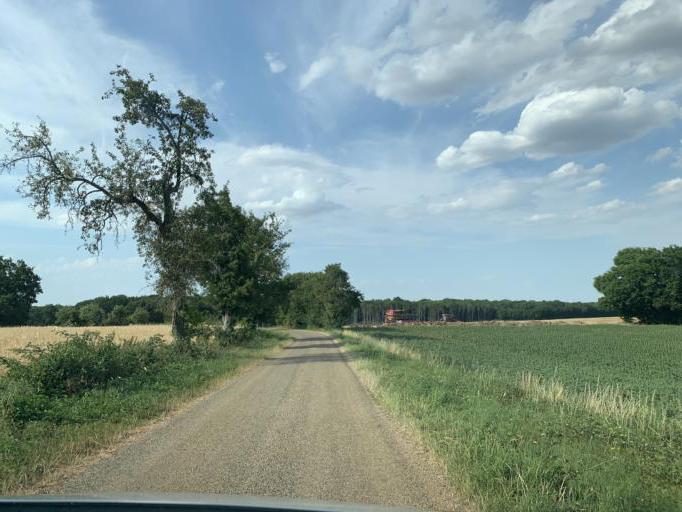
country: FR
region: Bourgogne
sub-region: Departement de l'Yonne
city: Fontenailles
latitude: 47.5028
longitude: 3.4294
